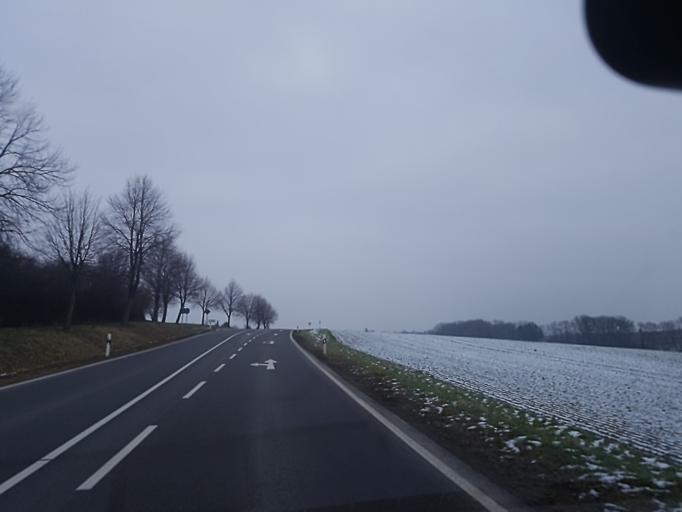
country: DE
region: Saxony
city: Mugeln
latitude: 51.2289
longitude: 13.0204
